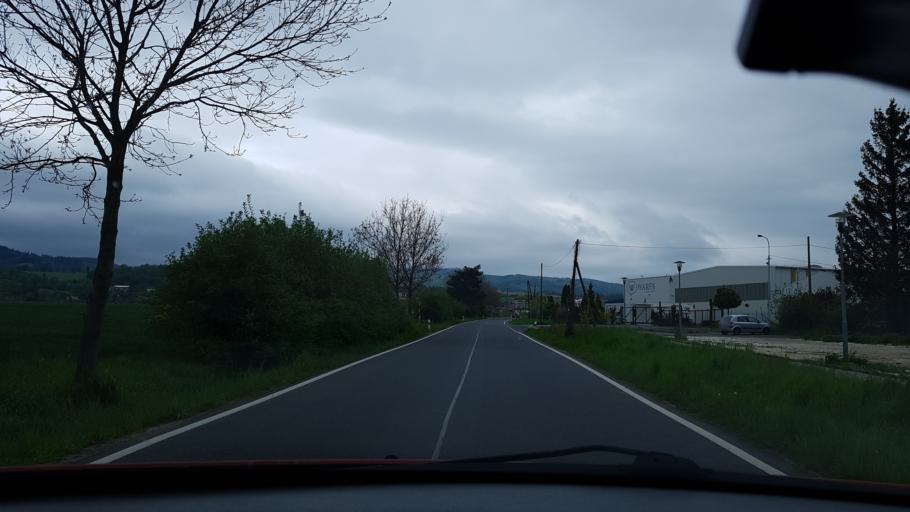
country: CZ
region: Olomoucky
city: Javornik
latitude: 50.3917
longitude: 17.0221
